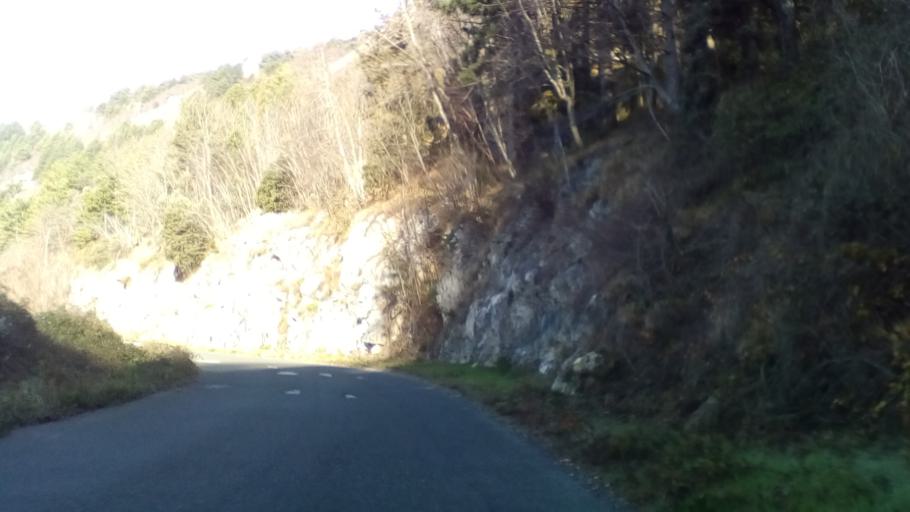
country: IT
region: Tuscany
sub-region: Provincia di Massa-Carrara
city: Montignoso
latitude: 44.0559
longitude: 10.2056
